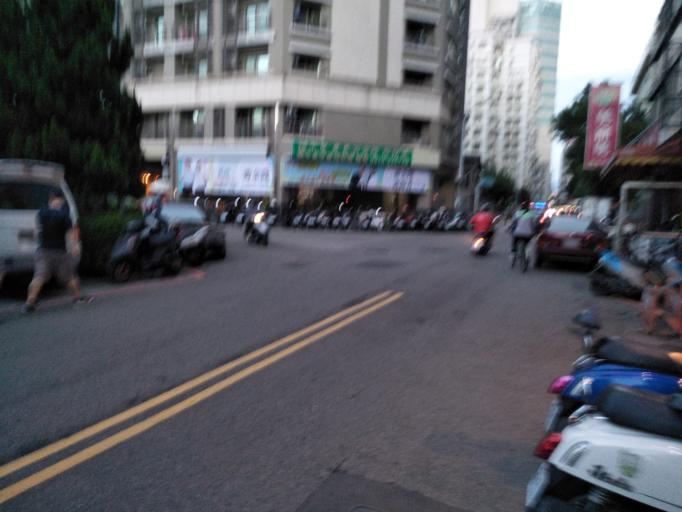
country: TW
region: Taiwan
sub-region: Taichung City
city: Taichung
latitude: 24.1522
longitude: 120.6829
